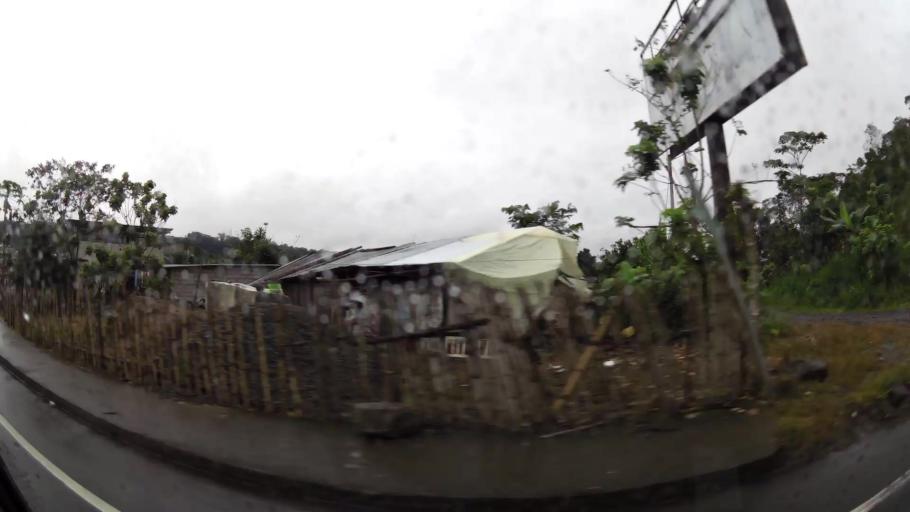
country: EC
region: Santo Domingo de los Tsachilas
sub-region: Canton Santo Domingo de los Colorados
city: Santo Domingo de los Colorados
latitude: -0.2425
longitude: -79.1352
